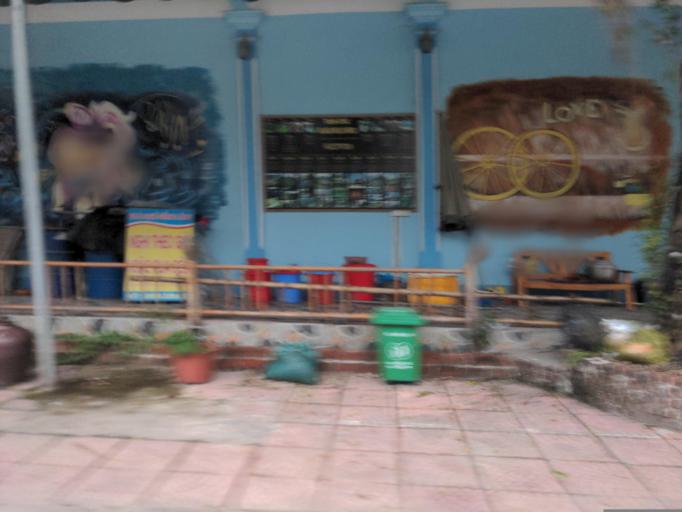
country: VN
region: Ninh Binh
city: Thi Tran Tam Diep
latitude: 20.2139
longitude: 105.9339
